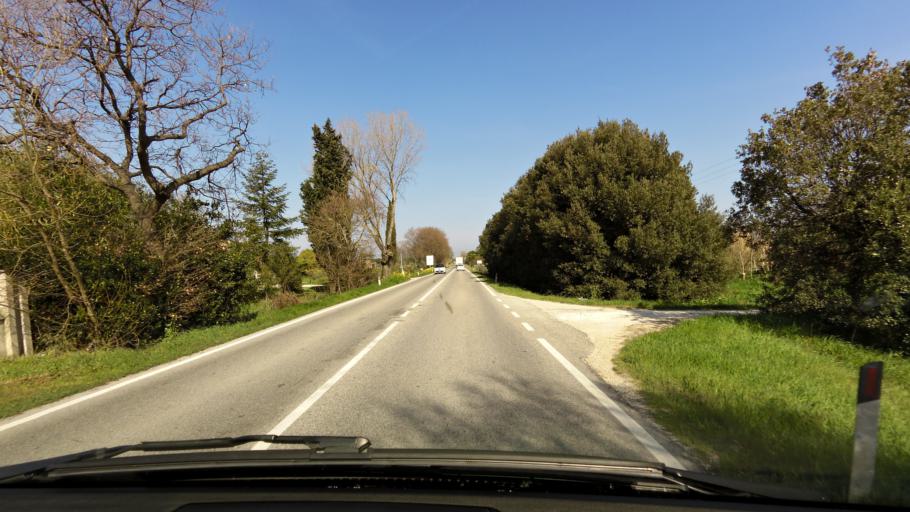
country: IT
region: The Marches
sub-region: Provincia di Macerata
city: Potenza Picena
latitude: 43.3962
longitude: 13.6474
